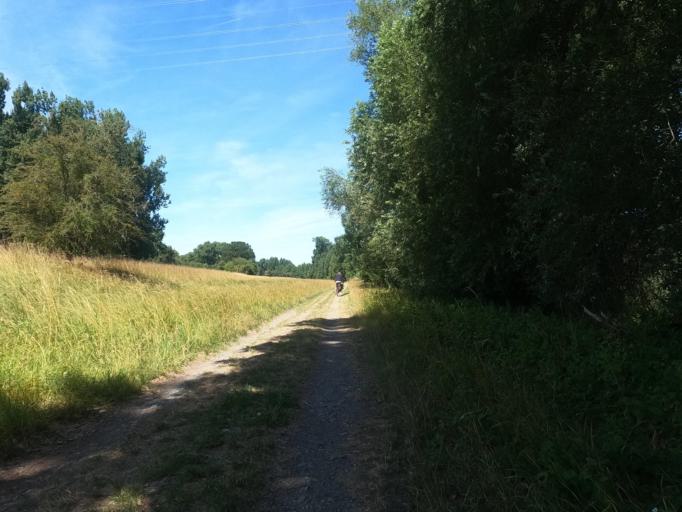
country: DE
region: Hesse
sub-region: Regierungsbezirk Darmstadt
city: Ginsheim-Gustavsburg
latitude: 49.9568
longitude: 8.3486
